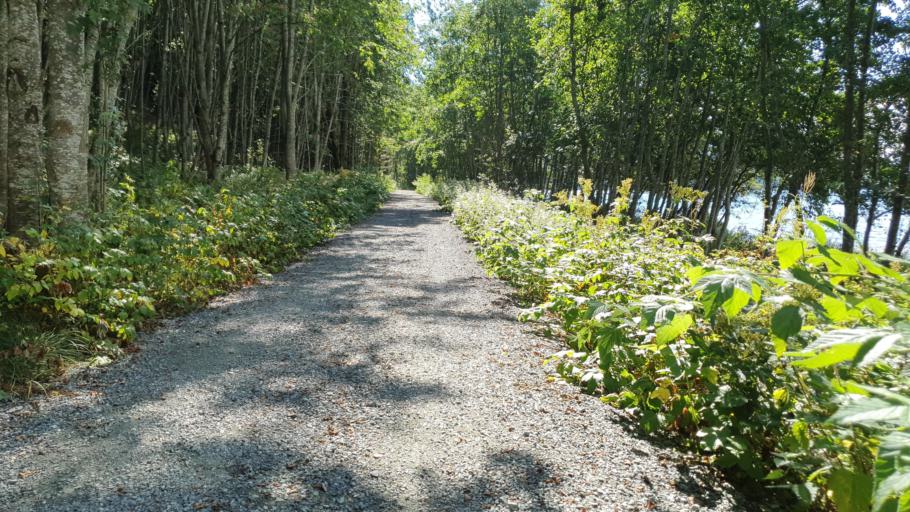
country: NO
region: Nord-Trondelag
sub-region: Levanger
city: Levanger
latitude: 63.7766
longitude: 11.3792
